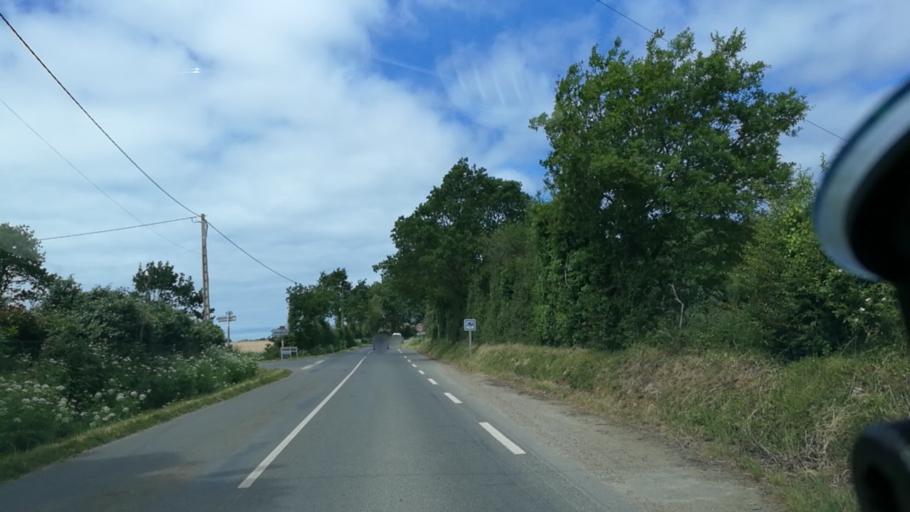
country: FR
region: Pays de la Loire
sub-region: Departement de la Loire-Atlantique
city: Asserac
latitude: 47.4396
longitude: -2.4314
